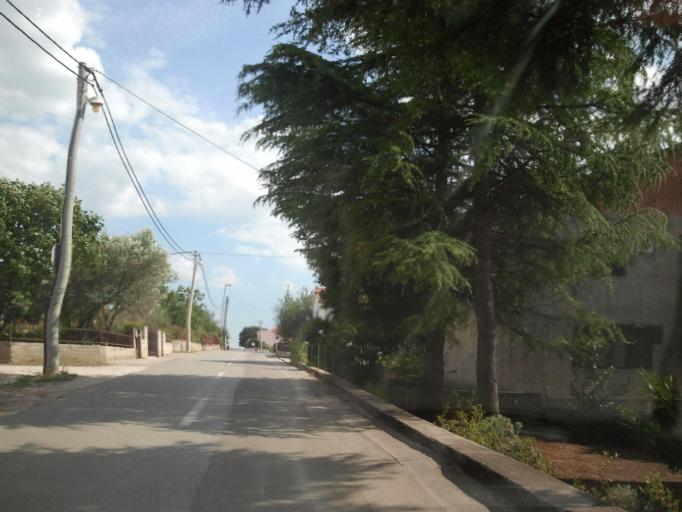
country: HR
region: Zadarska
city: Zadar
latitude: 44.1221
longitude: 15.2494
